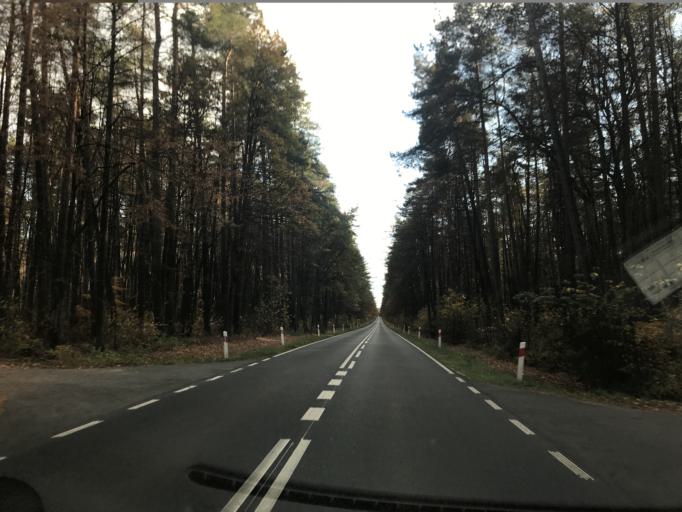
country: PL
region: Warmian-Masurian Voivodeship
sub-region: Powiat dzialdowski
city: Lidzbark
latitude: 53.3297
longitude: 19.8173
